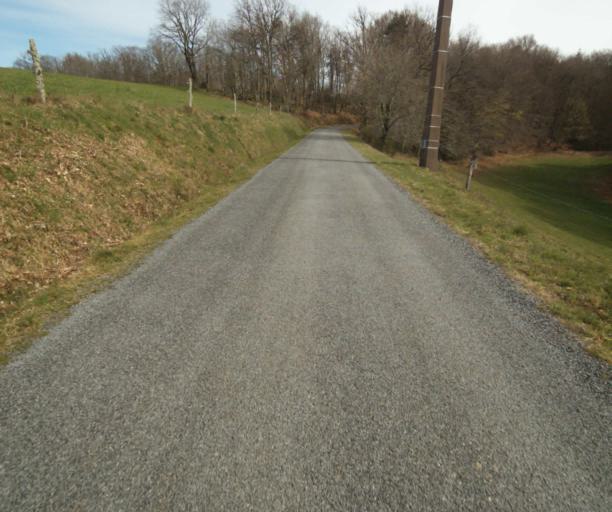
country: FR
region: Limousin
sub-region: Departement de la Correze
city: Correze
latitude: 45.3932
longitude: 1.8265
